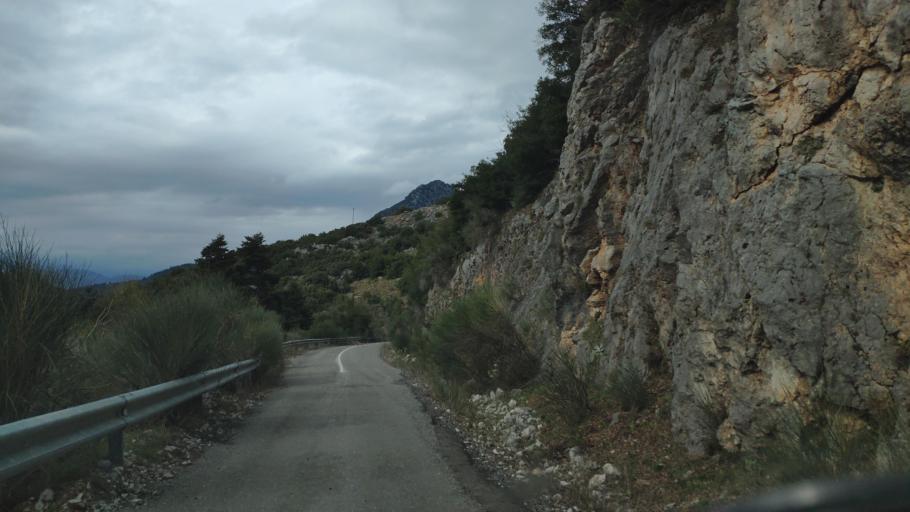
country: GR
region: Central Greece
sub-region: Nomos Fokidos
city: Amfissa
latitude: 38.6406
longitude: 22.4189
